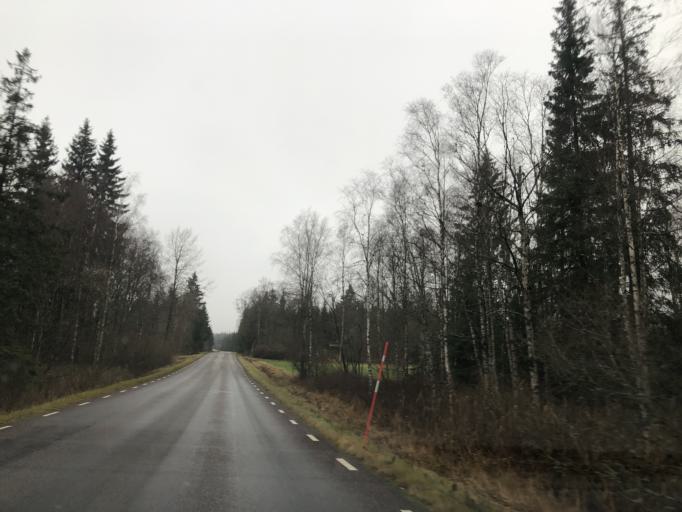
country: SE
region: Vaestra Goetaland
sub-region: Ulricehamns Kommun
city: Ulricehamn
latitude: 57.7455
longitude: 13.5326
